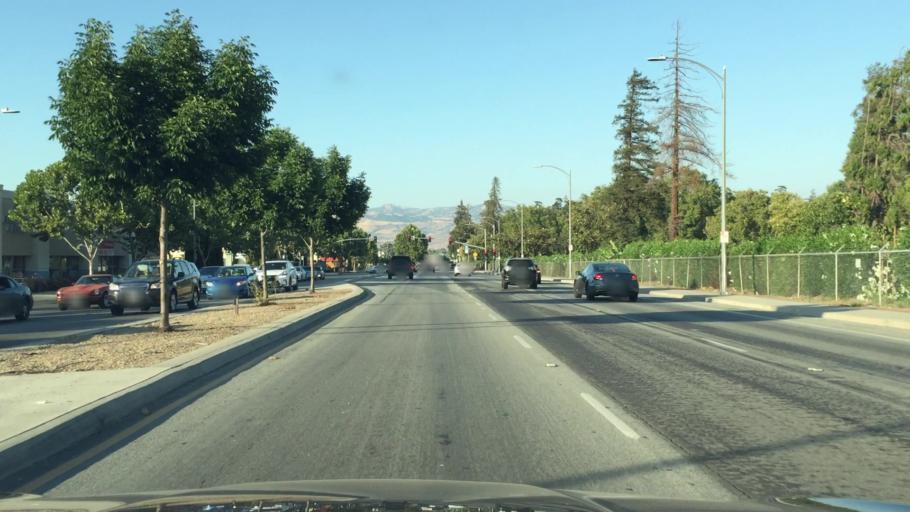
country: US
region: California
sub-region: Santa Clara County
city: Seven Trees
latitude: 37.3004
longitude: -121.8659
